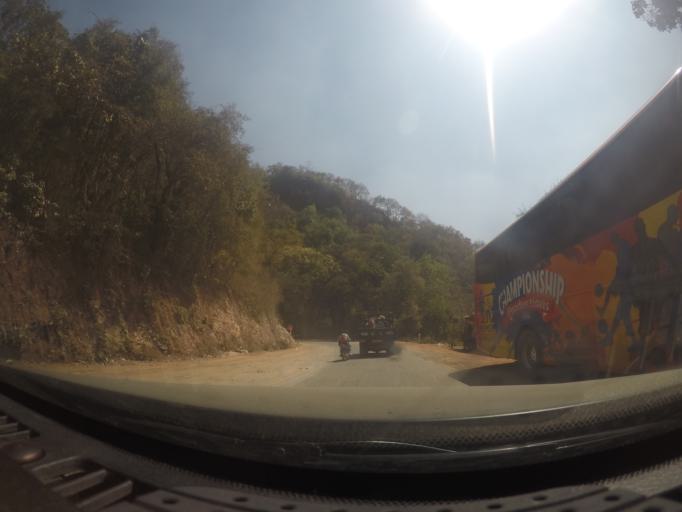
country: MM
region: Shan
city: Taunggyi
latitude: 20.8173
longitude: 97.2235
